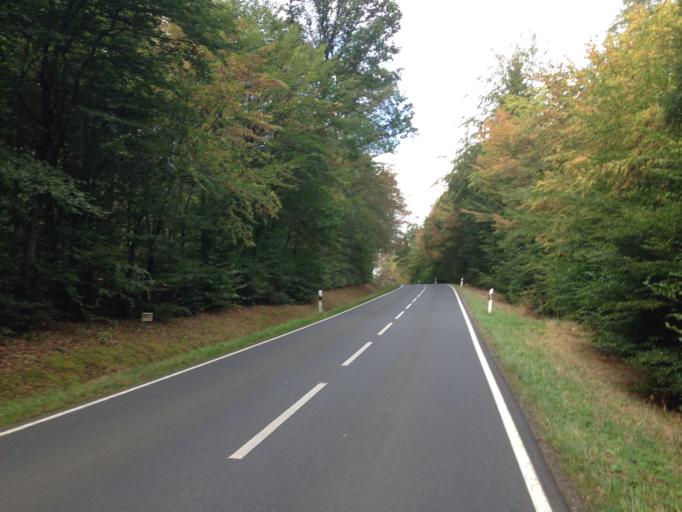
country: DE
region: Hesse
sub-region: Regierungsbezirk Giessen
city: Bad Endbach
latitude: 50.6733
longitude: 8.5473
